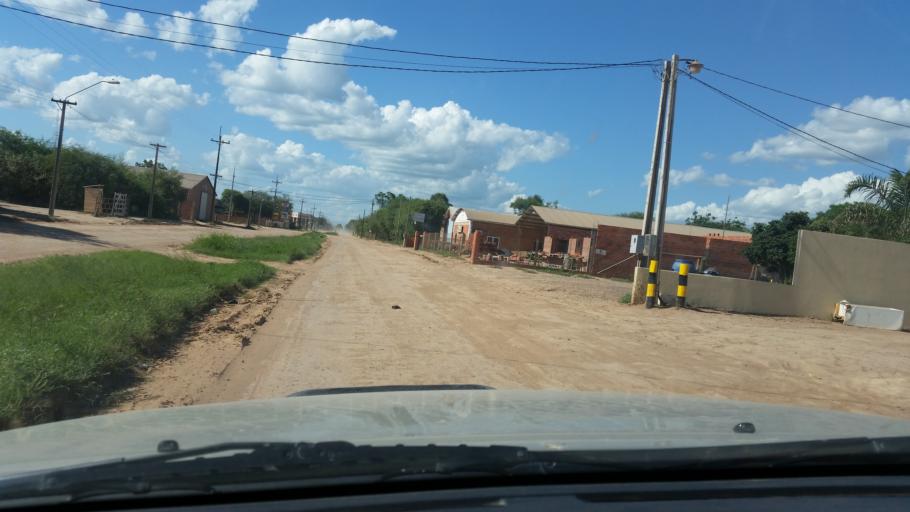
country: PY
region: Boqueron
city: Filadelfia
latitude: -22.3634
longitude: -60.0309
